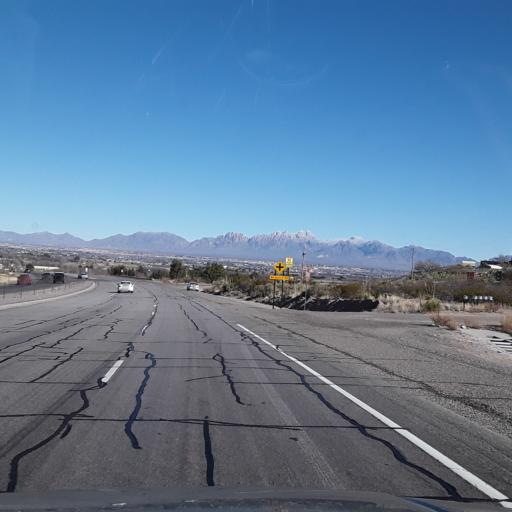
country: US
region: New Mexico
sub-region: Dona Ana County
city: Mesilla
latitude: 32.2931
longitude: -106.8623
